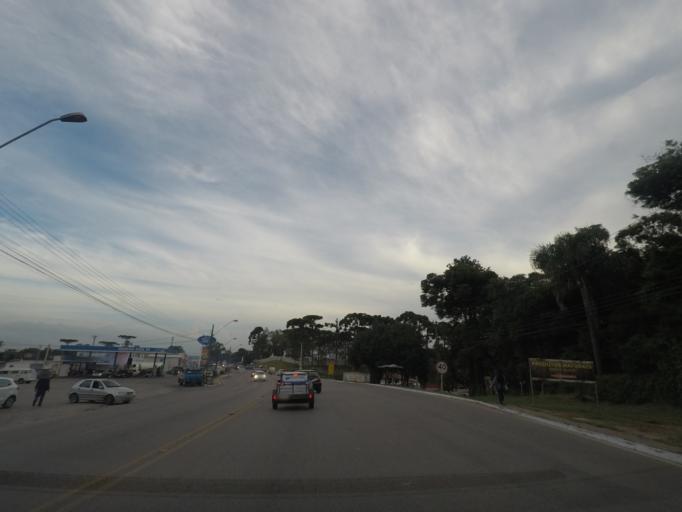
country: BR
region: Parana
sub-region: Colombo
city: Colombo
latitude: -25.3476
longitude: -49.2209
